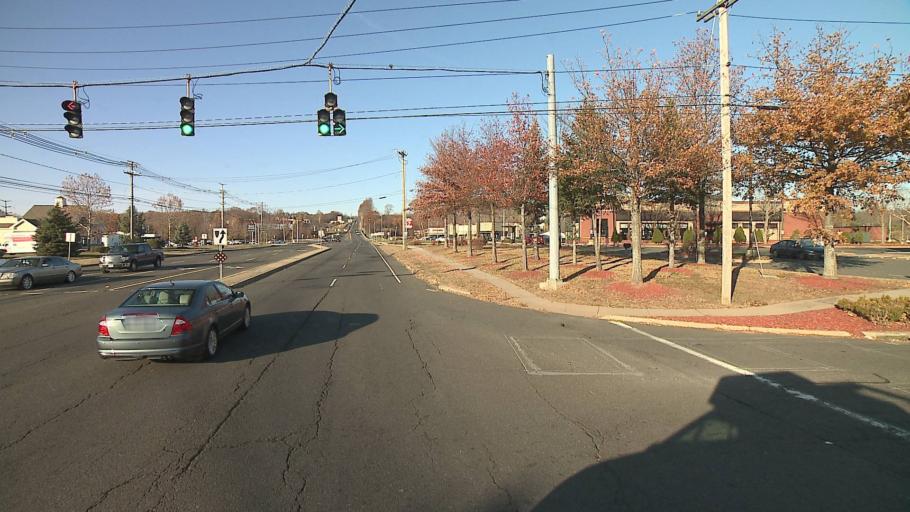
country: US
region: Connecticut
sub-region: New Haven County
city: Wallingford
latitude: 41.4963
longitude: -72.8096
